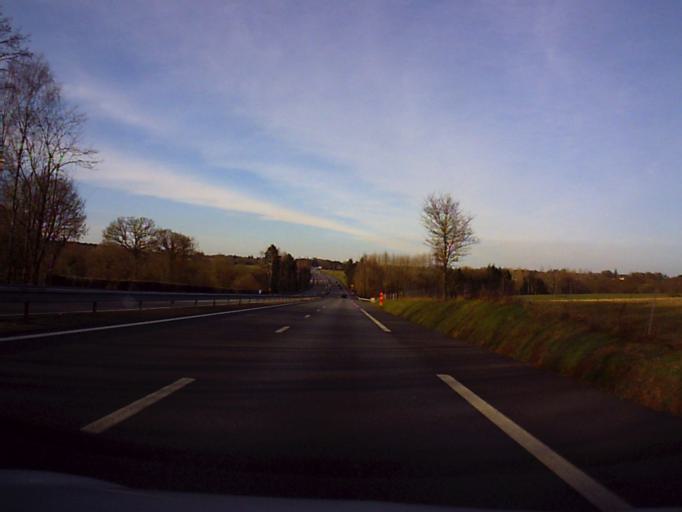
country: FR
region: Brittany
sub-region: Departement du Morbihan
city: Ploermel
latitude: 47.8892
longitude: -2.4144
